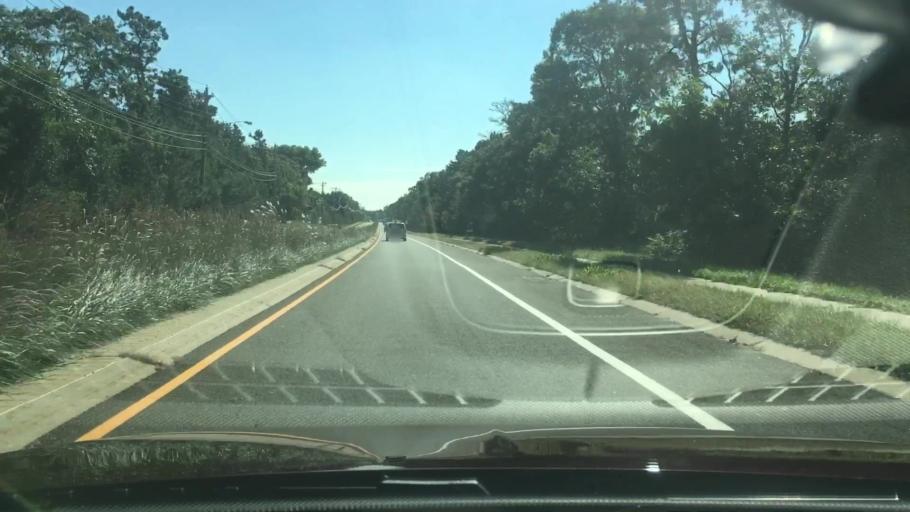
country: US
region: New York
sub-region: Suffolk County
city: Selden
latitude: 40.8985
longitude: -73.0209
